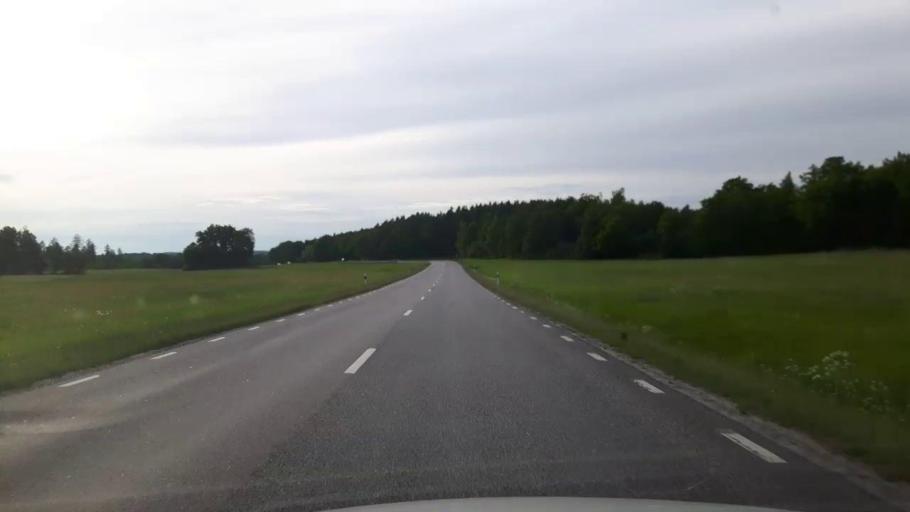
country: SE
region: Uppsala
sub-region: Habo Kommun
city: Balsta
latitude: 59.6477
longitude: 17.4273
